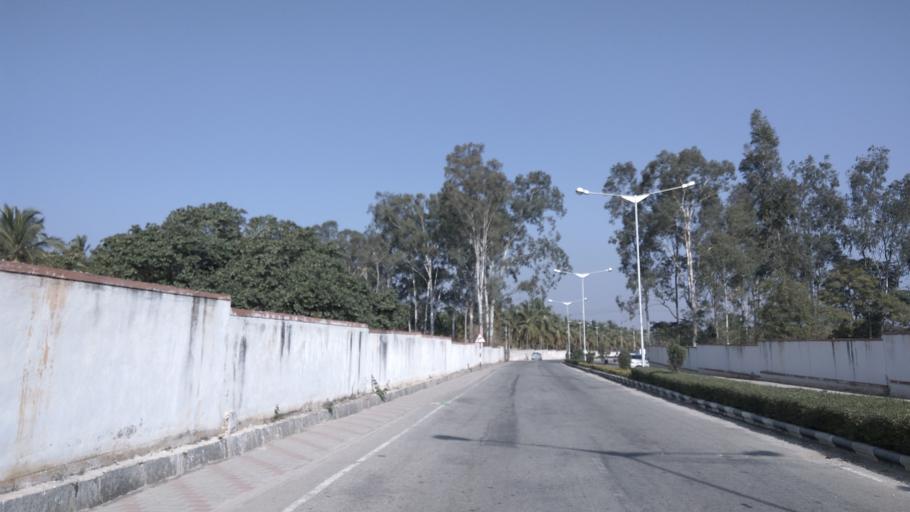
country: IN
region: Karnataka
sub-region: Bangalore Rural
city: Devanhalli
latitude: 13.1941
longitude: 77.6444
